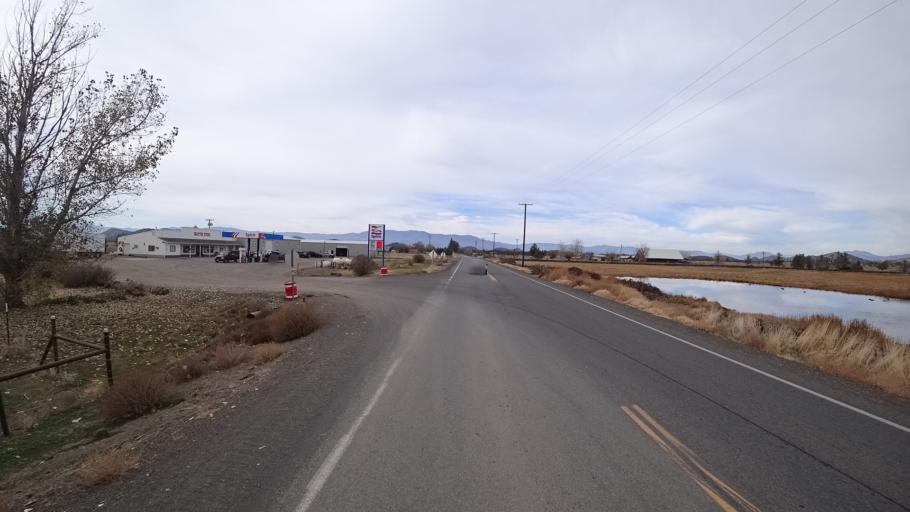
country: US
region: California
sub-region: Siskiyou County
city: Montague
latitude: 41.6240
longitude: -122.4071
